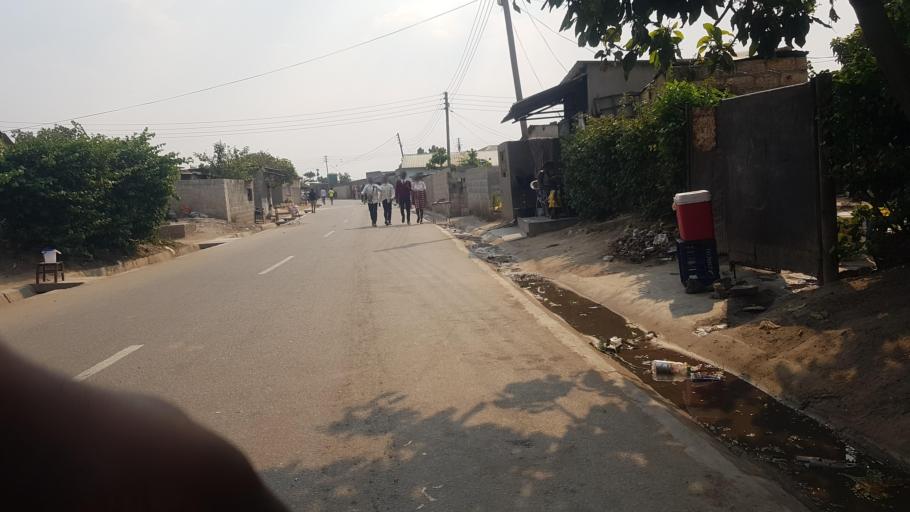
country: ZM
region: Lusaka
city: Lusaka
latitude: -15.4451
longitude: 28.3758
